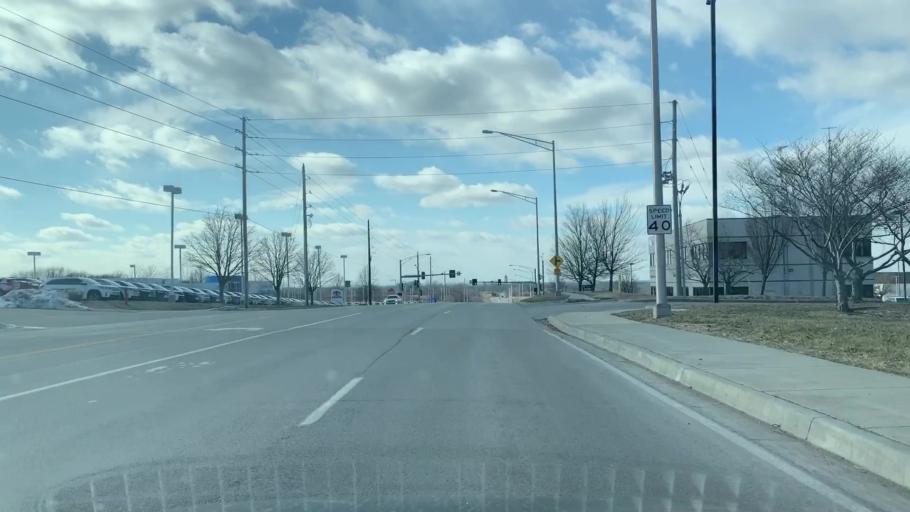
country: US
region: Missouri
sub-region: Jackson County
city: Lees Summit
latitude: 38.9464
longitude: -94.3679
